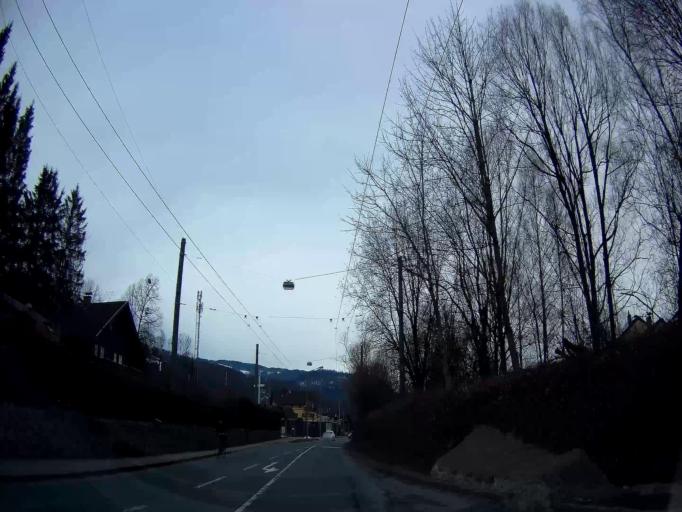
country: AT
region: Salzburg
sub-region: Politischer Bezirk Salzburg-Umgebung
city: Elsbethen
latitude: 47.7828
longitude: 13.0812
